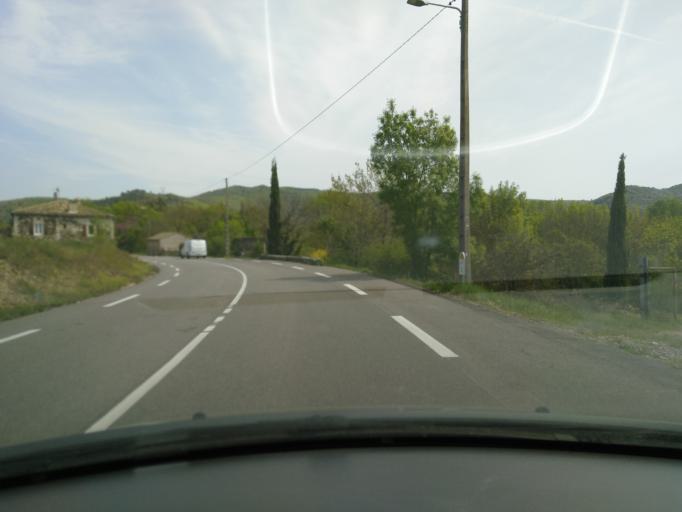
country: FR
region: Rhone-Alpes
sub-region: Departement de l'Ardeche
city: Lavilledieu
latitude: 44.5487
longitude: 4.4388
